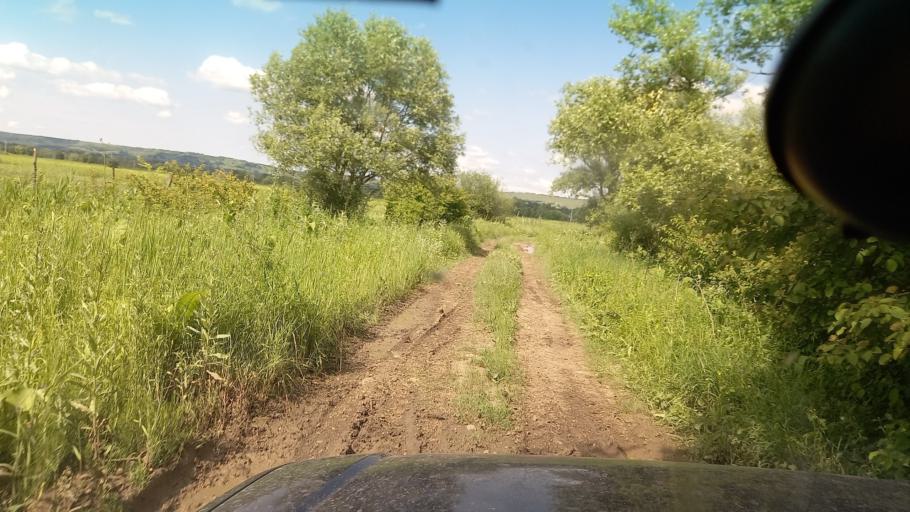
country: RU
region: Krasnodarskiy
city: Shedok
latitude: 44.2115
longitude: 40.9725
